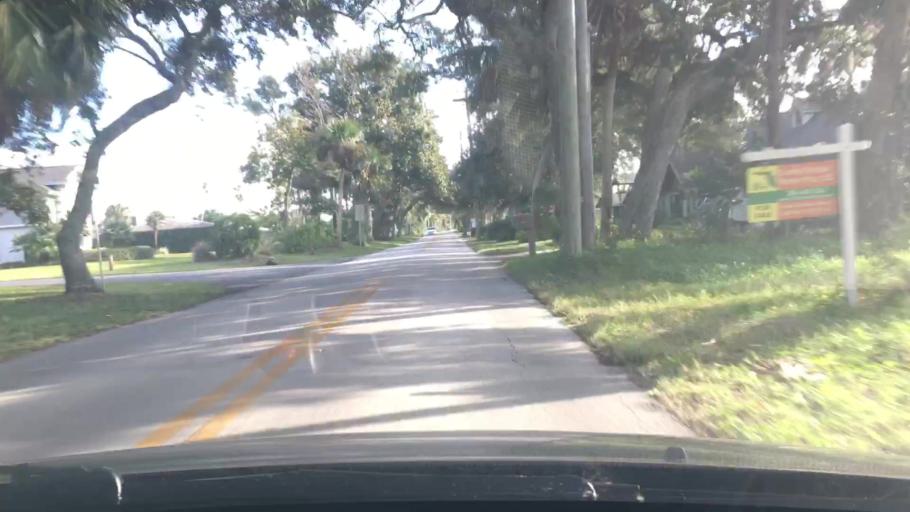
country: US
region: Florida
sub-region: Volusia County
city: Ormond-by-the-Sea
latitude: 29.3615
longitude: -81.0789
